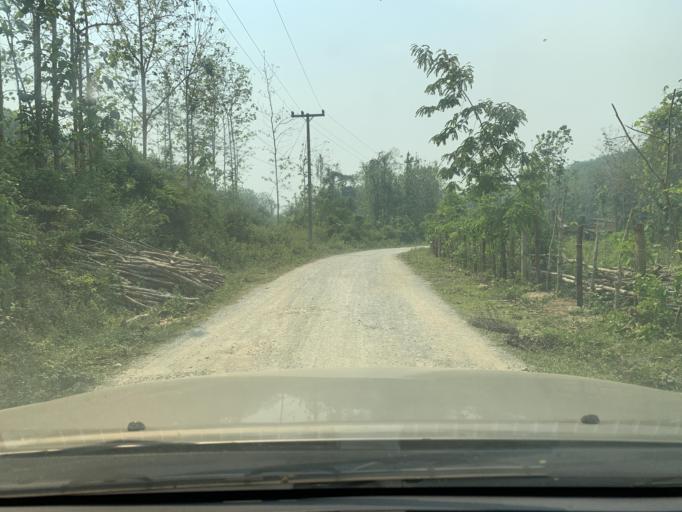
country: LA
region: Louangphabang
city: Louangphabang
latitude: 19.8822
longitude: 102.2591
